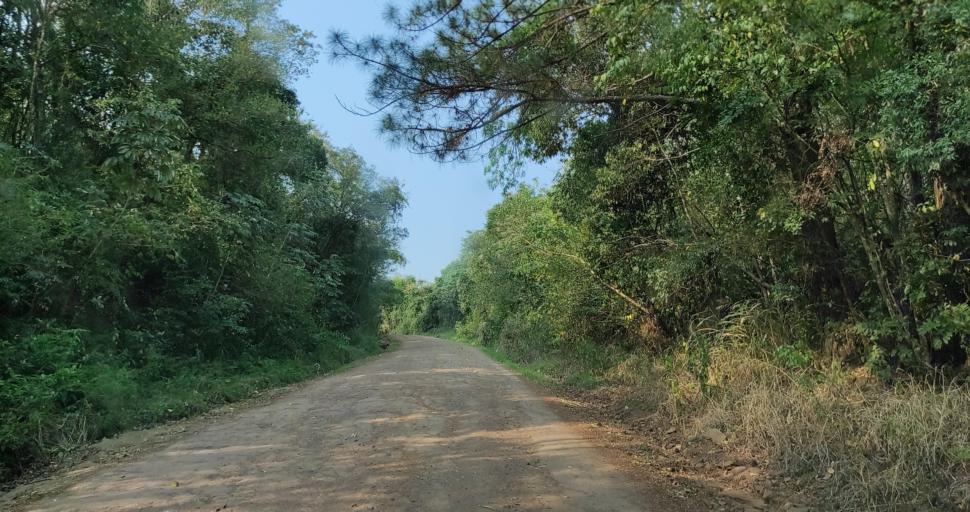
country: AR
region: Misiones
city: Cerro Azul
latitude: -27.6267
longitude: -55.5306
